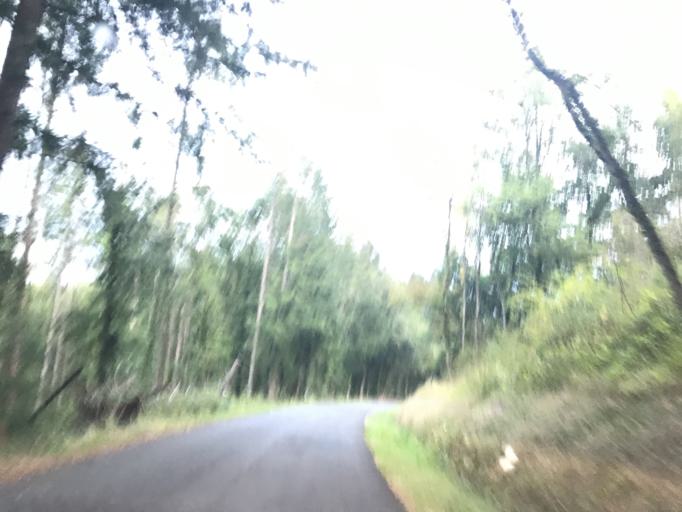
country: FR
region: Auvergne
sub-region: Departement du Puy-de-Dome
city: Escoutoux
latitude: 45.7829
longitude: 3.5850
